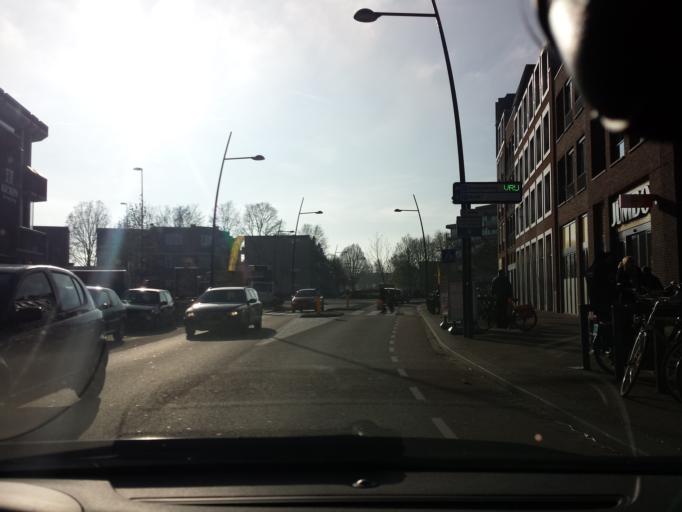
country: NL
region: Limburg
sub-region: Gemeente Heerlen
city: Heerlen
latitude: 50.8921
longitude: 6.0154
